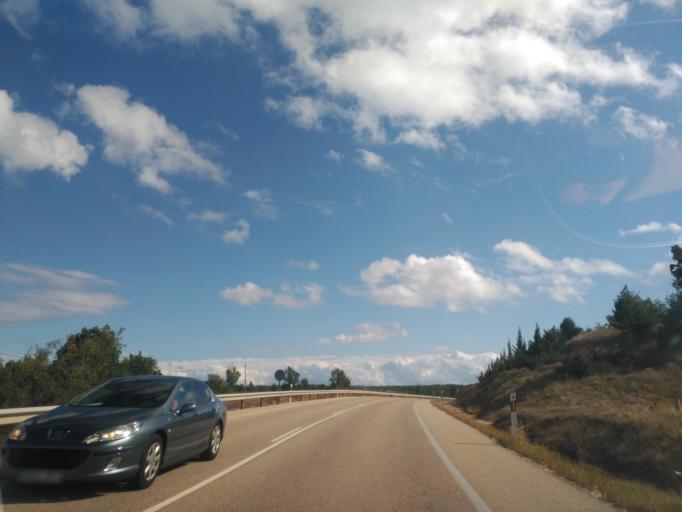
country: ES
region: Castille and Leon
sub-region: Provincia de Burgos
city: Hacinas
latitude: 41.9624
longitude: -3.2921
